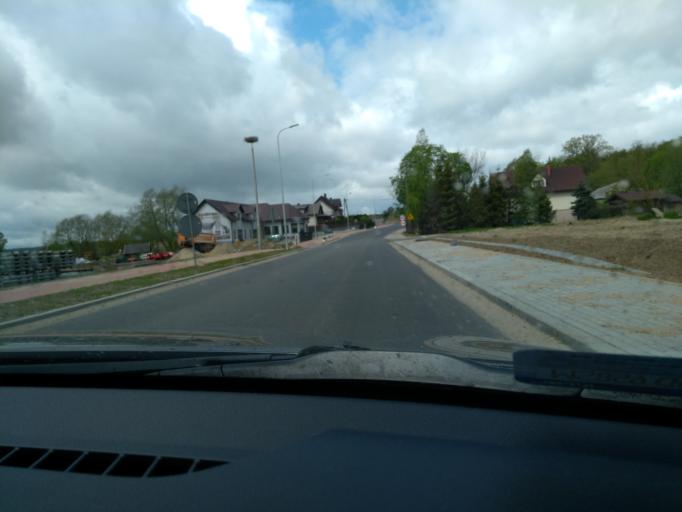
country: PL
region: Pomeranian Voivodeship
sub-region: Powiat kartuski
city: Chmielno
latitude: 54.3419
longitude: 18.0555
